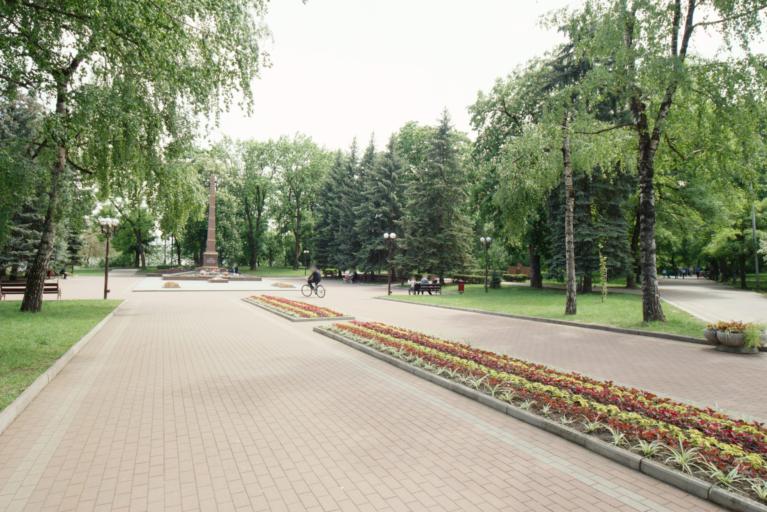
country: RU
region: Kabardino-Balkariya
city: Vol'nyy Aul
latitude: 43.4759
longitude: 43.6032
